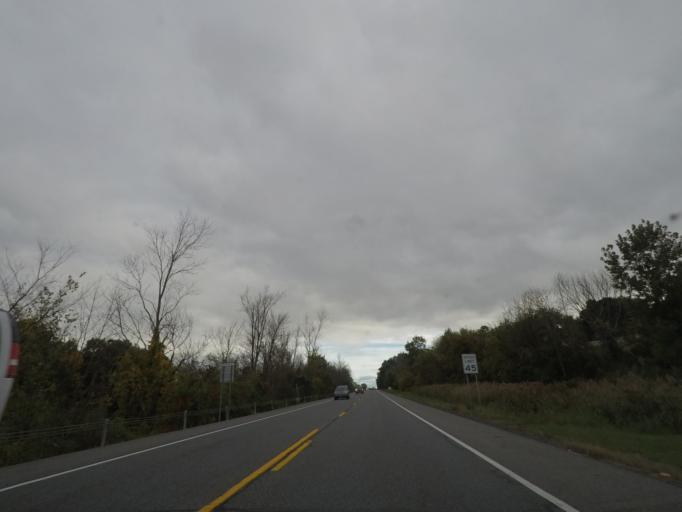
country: US
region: New York
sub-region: Saratoga County
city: Mechanicville
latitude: 42.8727
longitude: -73.7252
